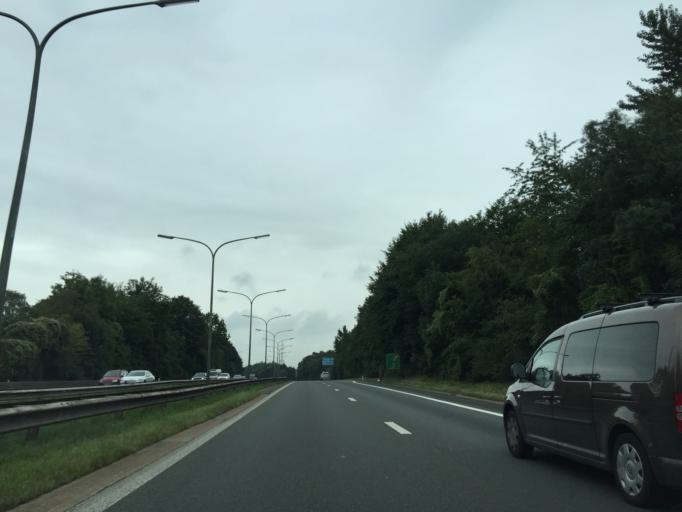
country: BE
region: Wallonia
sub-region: Province de Liege
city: Dison
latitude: 50.6008
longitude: 5.8486
